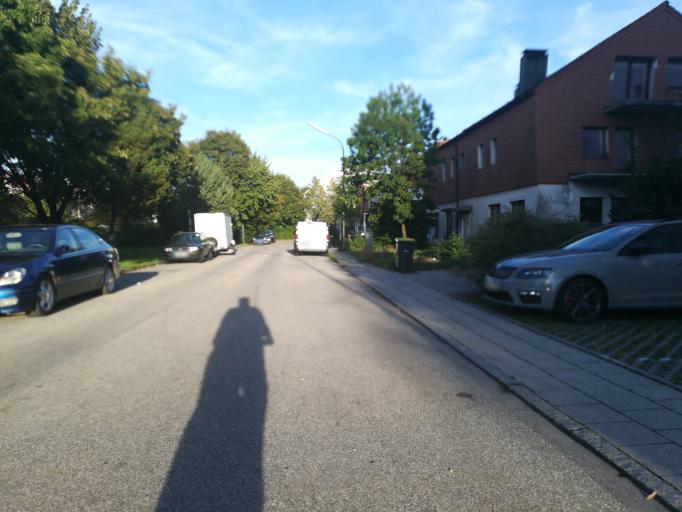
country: DE
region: Bavaria
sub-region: Upper Bavaria
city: Karlsfeld
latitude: 48.2296
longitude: 11.4855
